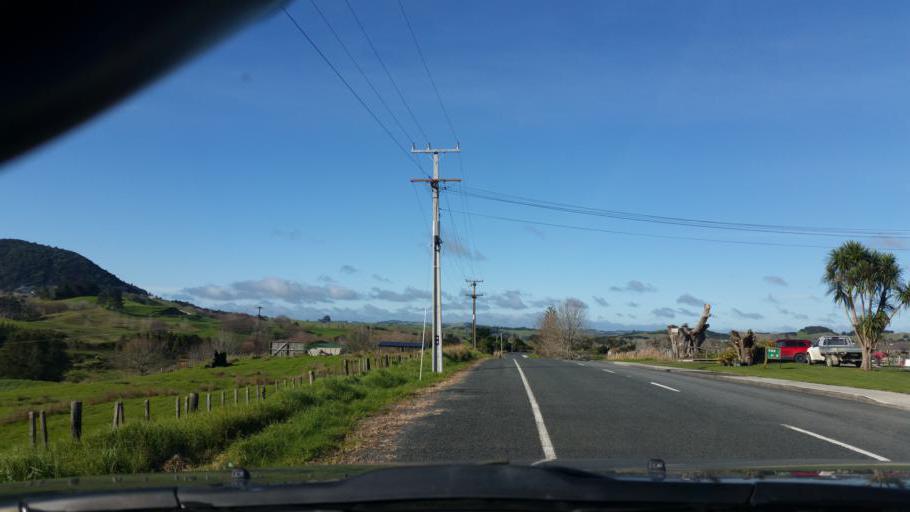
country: NZ
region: Northland
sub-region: Whangarei
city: Ruakaka
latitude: -36.1116
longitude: 174.3636
